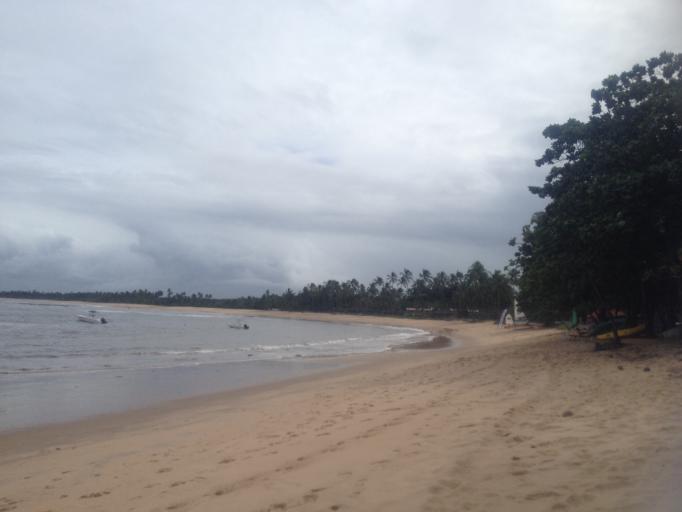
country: BR
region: Bahia
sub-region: Mata De Sao Joao
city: Mata de Sao Joao
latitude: -12.5817
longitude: -38.0097
